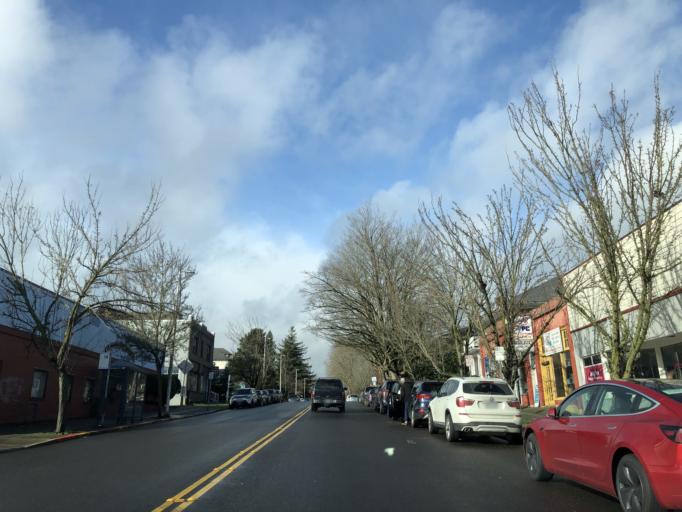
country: US
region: Washington
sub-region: Pierce County
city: Tacoma
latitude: 47.2623
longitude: -122.4520
